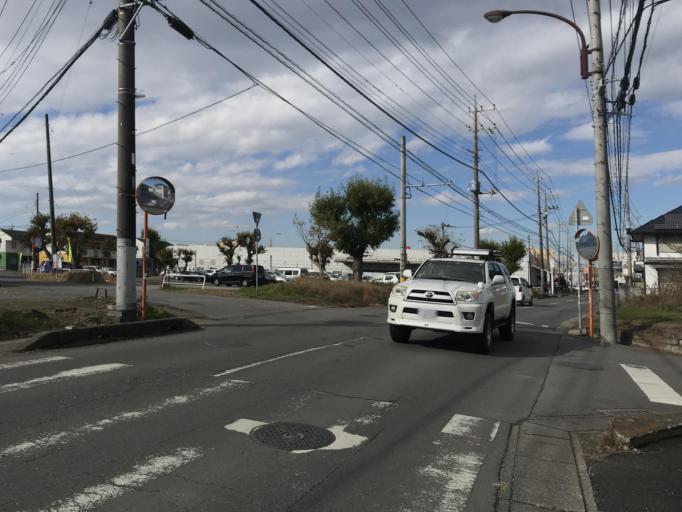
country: JP
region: Ibaraki
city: Ushiku
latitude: 35.9677
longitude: 140.1529
